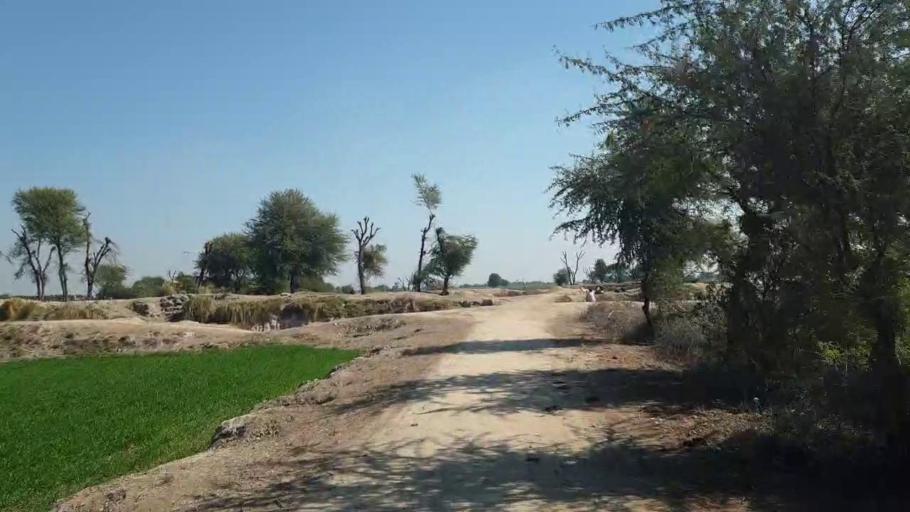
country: PK
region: Sindh
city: Shahpur Chakar
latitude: 26.1245
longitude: 68.6480
